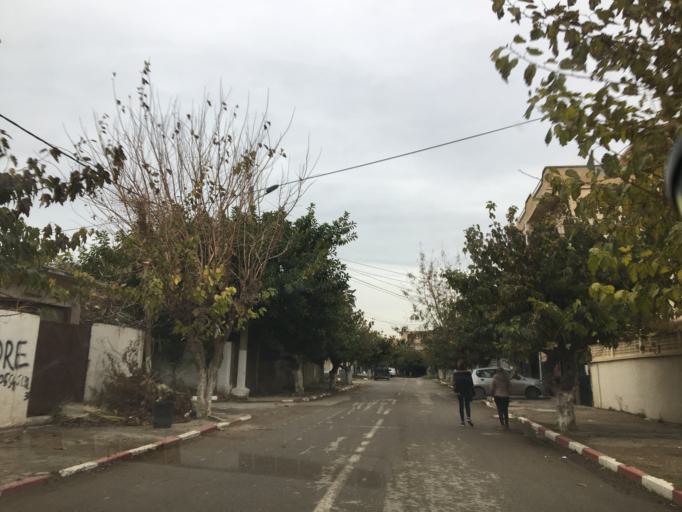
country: DZ
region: Alger
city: Ain Taya
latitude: 36.7935
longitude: 3.2375
